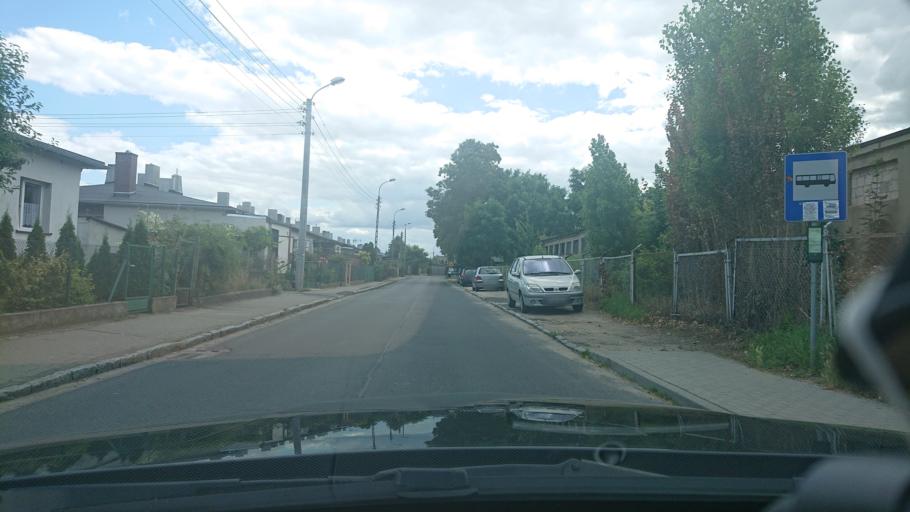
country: PL
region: Greater Poland Voivodeship
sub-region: Powiat gnieznienski
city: Gniezno
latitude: 52.5162
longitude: 17.6053
